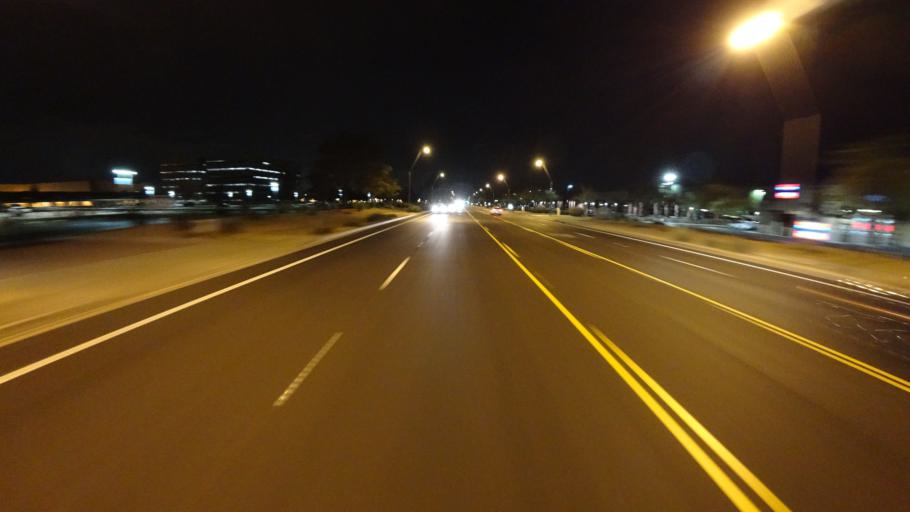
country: US
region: Arizona
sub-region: Maricopa County
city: Guadalupe
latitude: 33.3346
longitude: -111.9617
